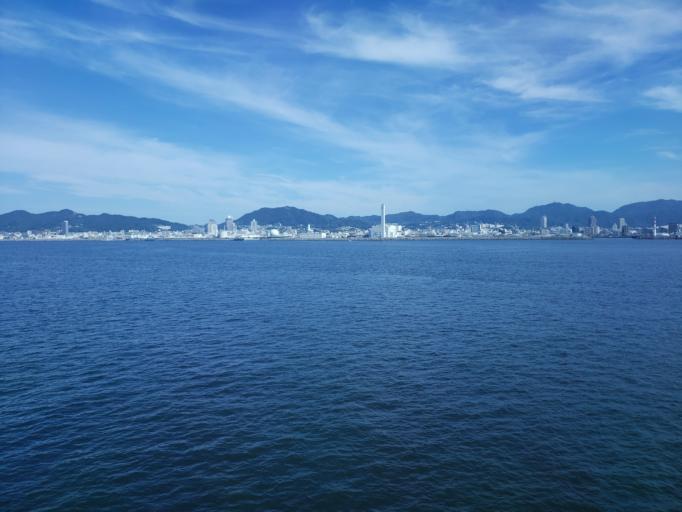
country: JP
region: Hyogo
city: Kobe
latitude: 34.6355
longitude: 135.1684
